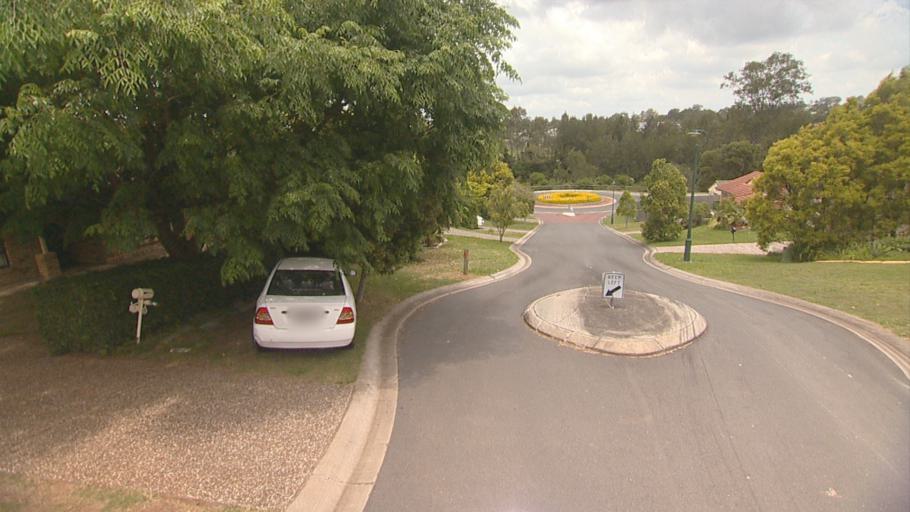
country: AU
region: Queensland
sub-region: Logan
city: Woodridge
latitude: -27.6154
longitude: 153.1051
